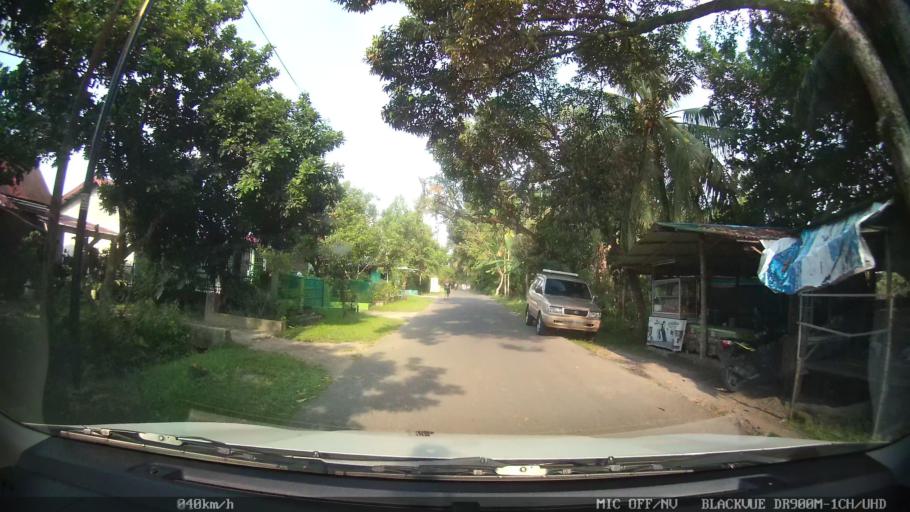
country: ID
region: North Sumatra
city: Binjai
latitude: 3.6030
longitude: 98.5040
